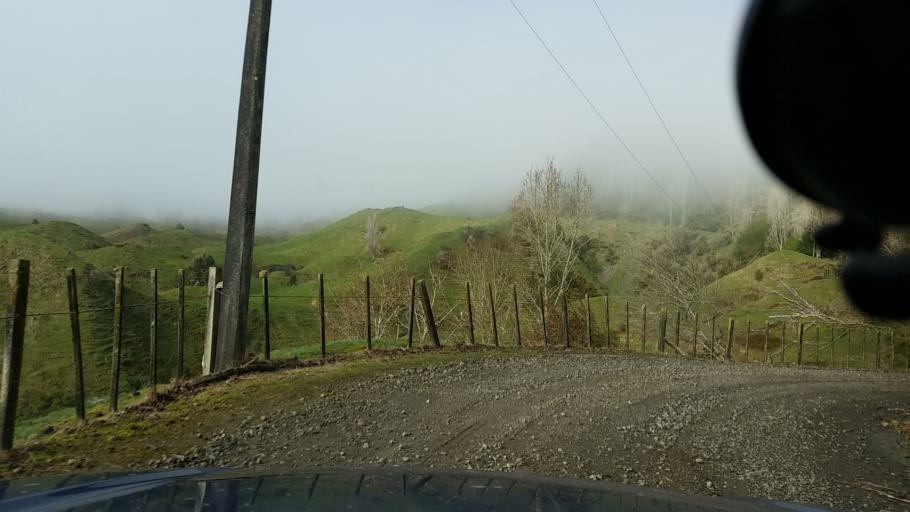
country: NZ
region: Taranaki
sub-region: New Plymouth District
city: Waitara
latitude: -39.0028
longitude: 174.7649
